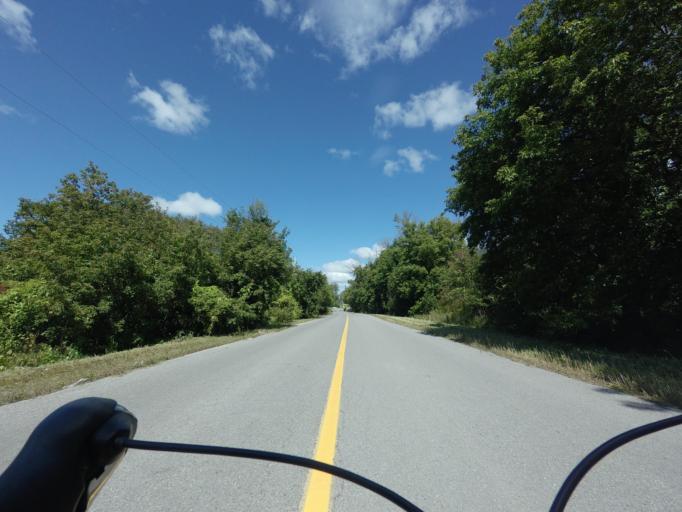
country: CA
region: Ontario
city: Bells Corners
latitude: 45.2537
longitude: -75.8091
